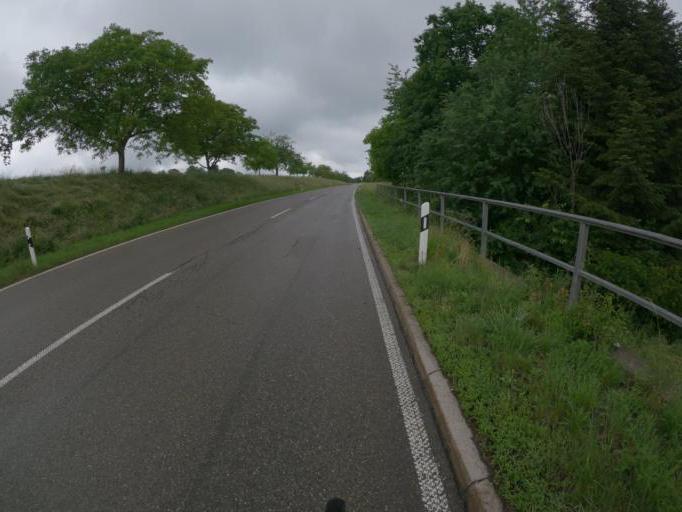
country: DE
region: Baden-Wuerttemberg
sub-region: Regierungsbezirk Stuttgart
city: Adelberg
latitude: 48.7556
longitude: 9.6043
